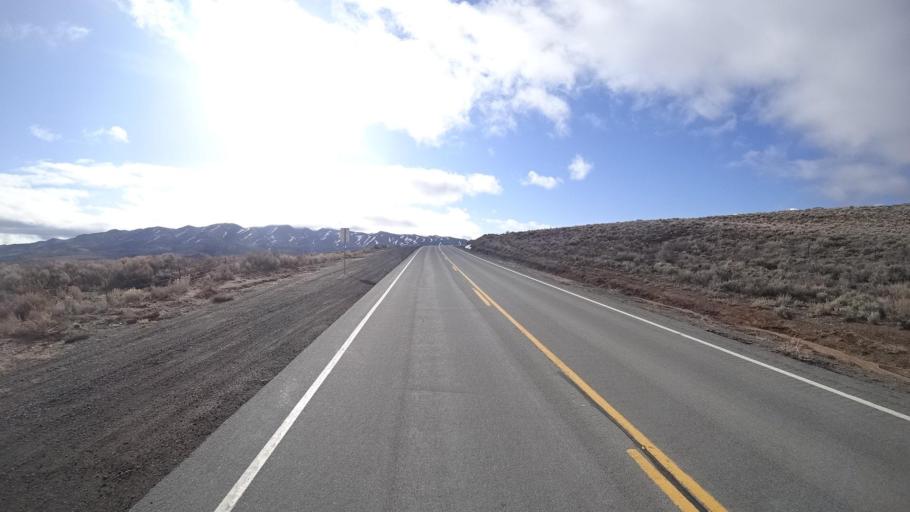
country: US
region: Nevada
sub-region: Washoe County
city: Cold Springs
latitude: 39.7989
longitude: -119.9022
